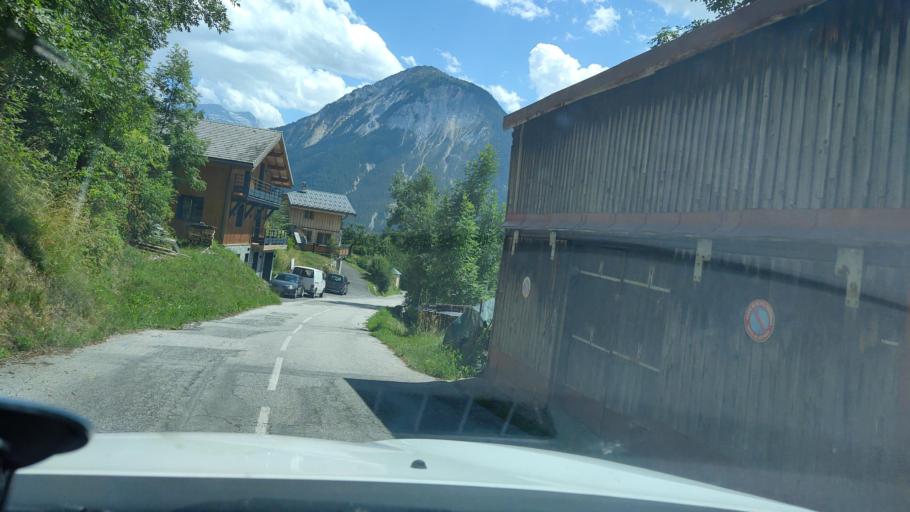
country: FR
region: Rhone-Alpes
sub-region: Departement de la Savoie
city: Bozel
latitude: 45.4524
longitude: 6.6541
